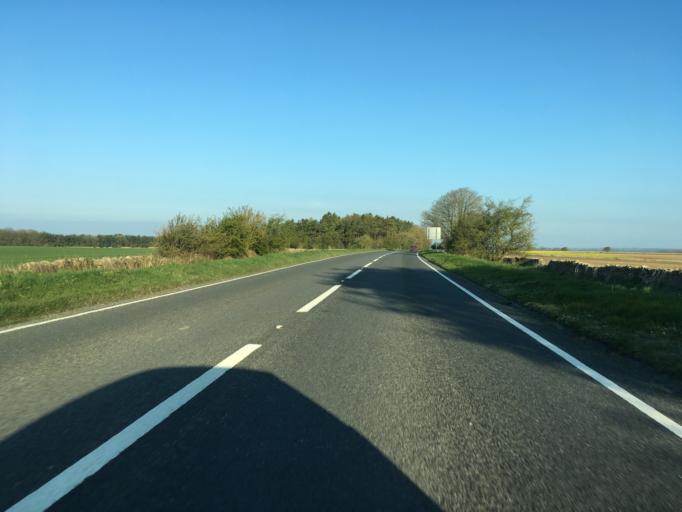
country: GB
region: England
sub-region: Gloucestershire
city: Bourton on the Water
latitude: 51.8121
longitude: -1.7308
